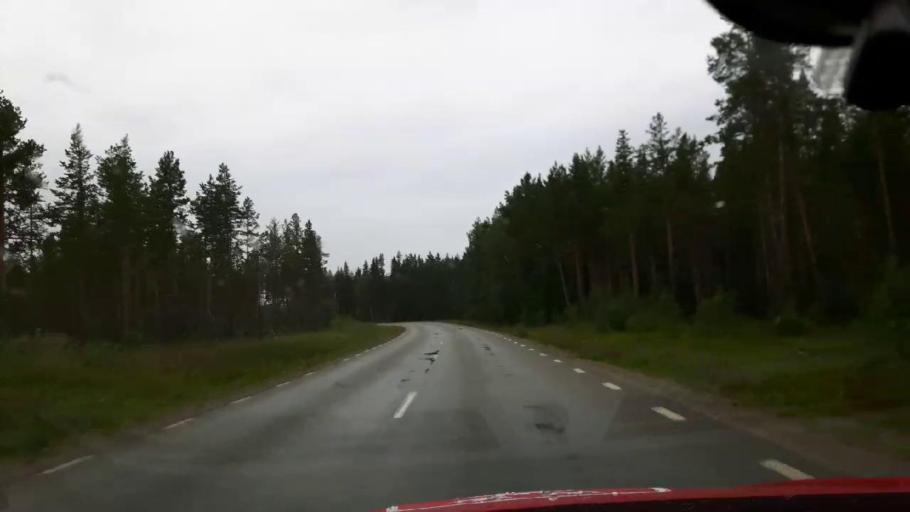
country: SE
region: Jaemtland
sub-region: OEstersunds Kommun
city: Brunflo
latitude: 62.8173
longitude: 14.9941
